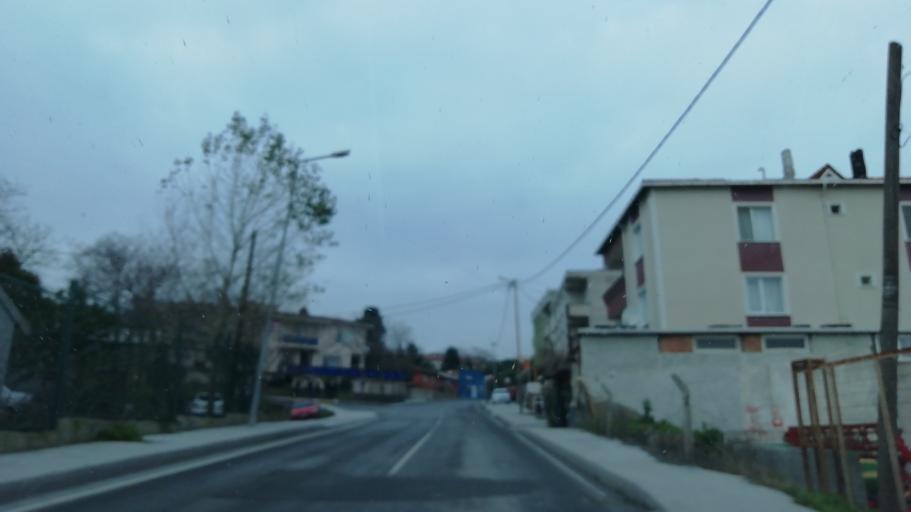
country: TR
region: Istanbul
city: Esenyurt
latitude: 41.1149
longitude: 28.6395
